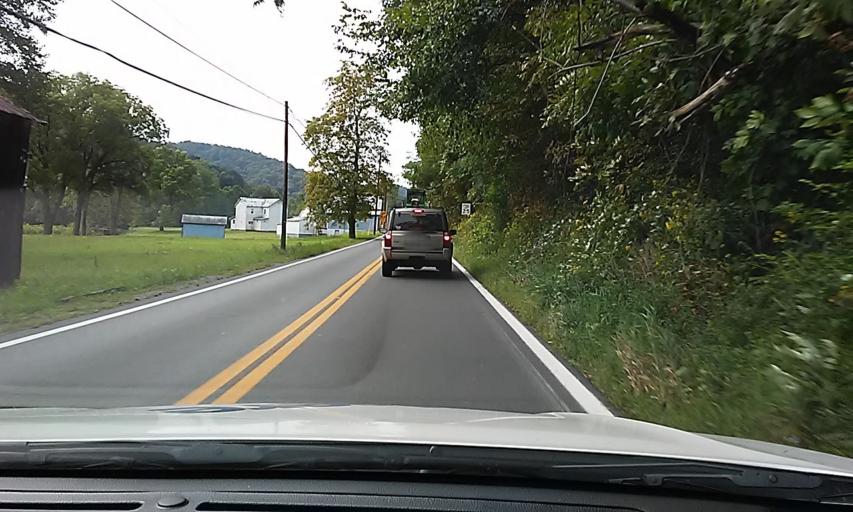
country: US
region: West Virginia
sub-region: Marion County
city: Mannington
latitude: 39.6771
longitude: -80.3382
